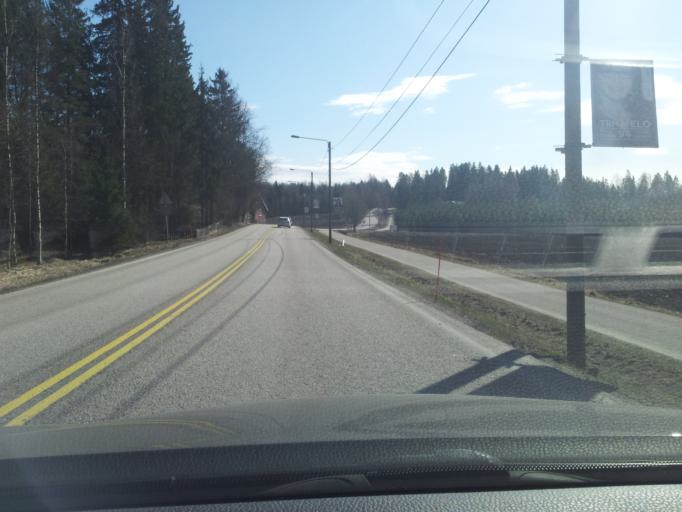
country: FI
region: Uusimaa
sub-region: Helsinki
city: Espoo
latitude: 60.1893
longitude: 24.6647
